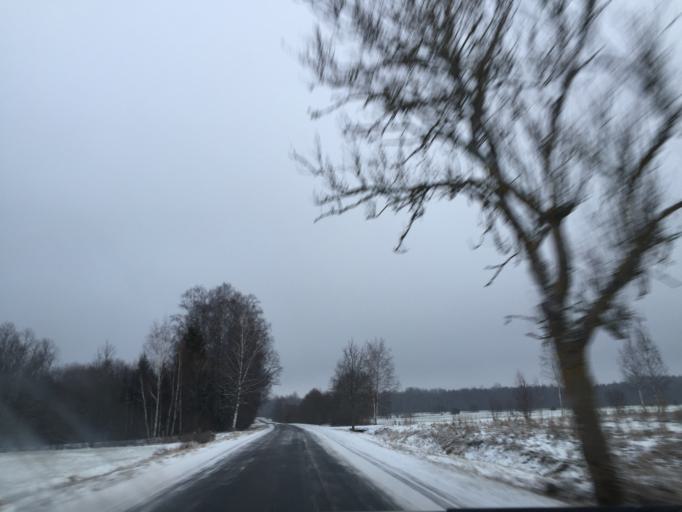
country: EE
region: Laeaene
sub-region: Lihula vald
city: Lihula
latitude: 58.5323
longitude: 24.0555
